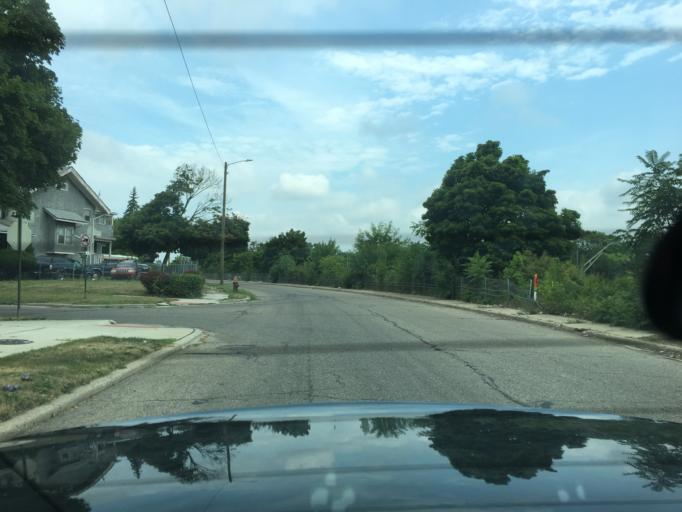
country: US
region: Michigan
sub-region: Wayne County
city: Highland Park
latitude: 42.3810
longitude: -83.0923
